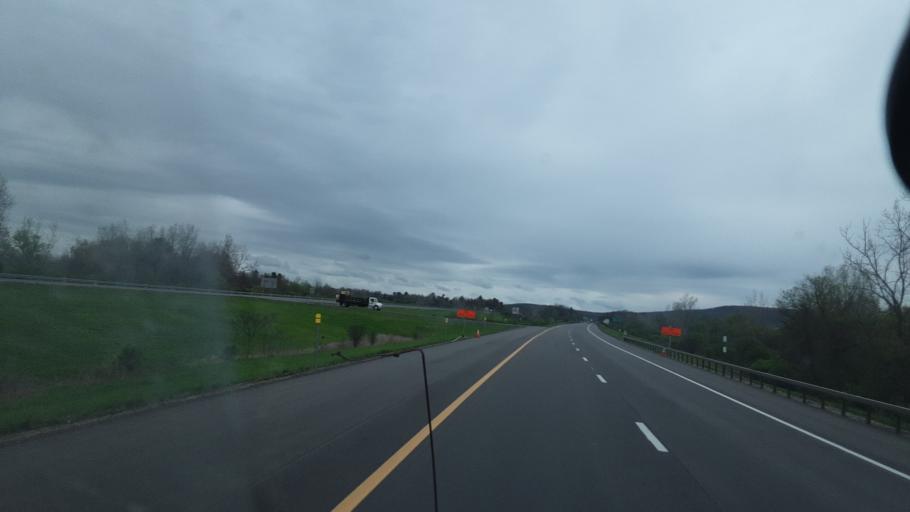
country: US
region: New York
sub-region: Allegany County
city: Belmont
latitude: 42.2661
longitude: -78.0566
